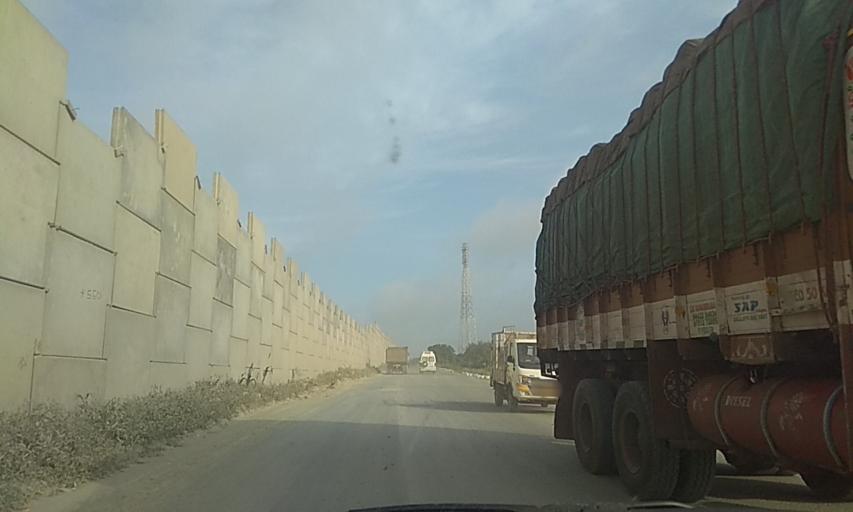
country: IN
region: Karnataka
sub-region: Haveri
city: Haveri
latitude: 14.7575
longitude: 75.4414
